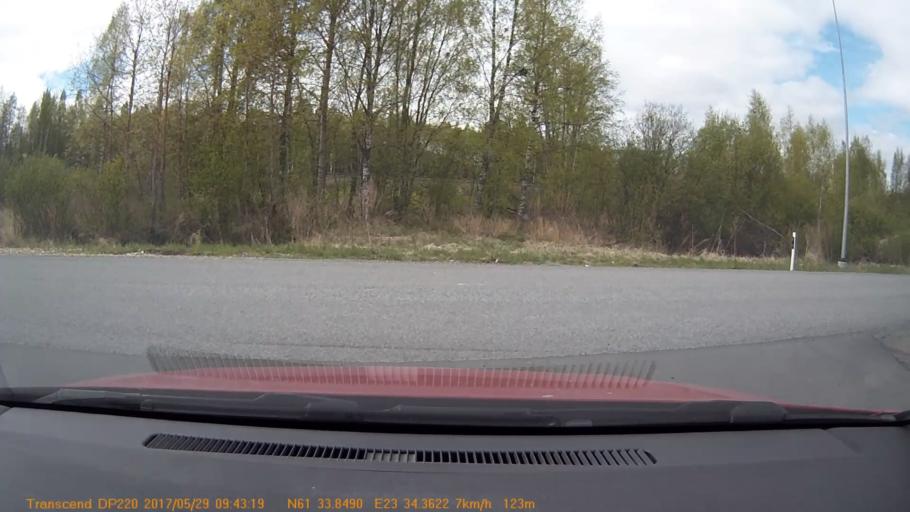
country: FI
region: Pirkanmaa
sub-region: Tampere
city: Yloejaervi
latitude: 61.5642
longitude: 23.5727
